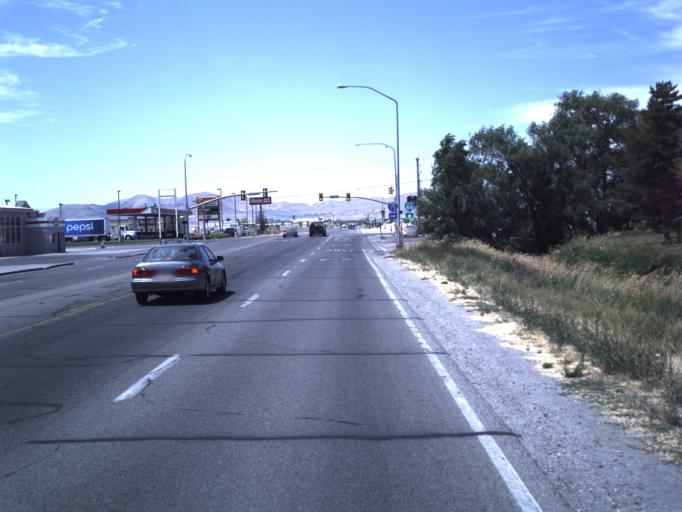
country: US
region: Utah
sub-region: Box Elder County
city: Tremonton
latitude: 41.7114
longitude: -112.1793
